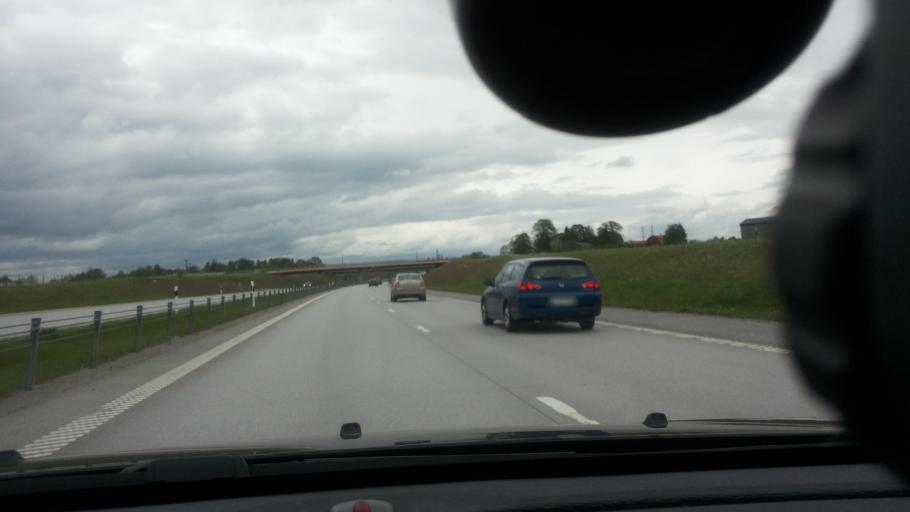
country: SE
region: Uppsala
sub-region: Uppsala Kommun
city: Gamla Uppsala
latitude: 59.9033
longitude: 17.6515
